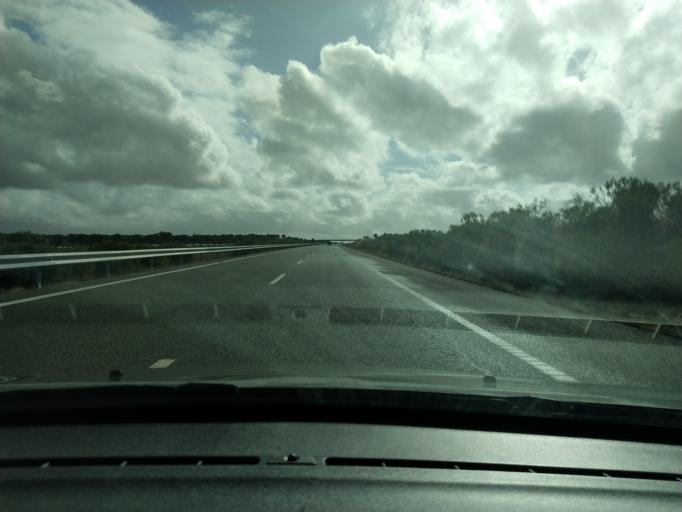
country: PT
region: Beja
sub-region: Ourique
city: Ourique
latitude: 37.6137
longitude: -8.1644
